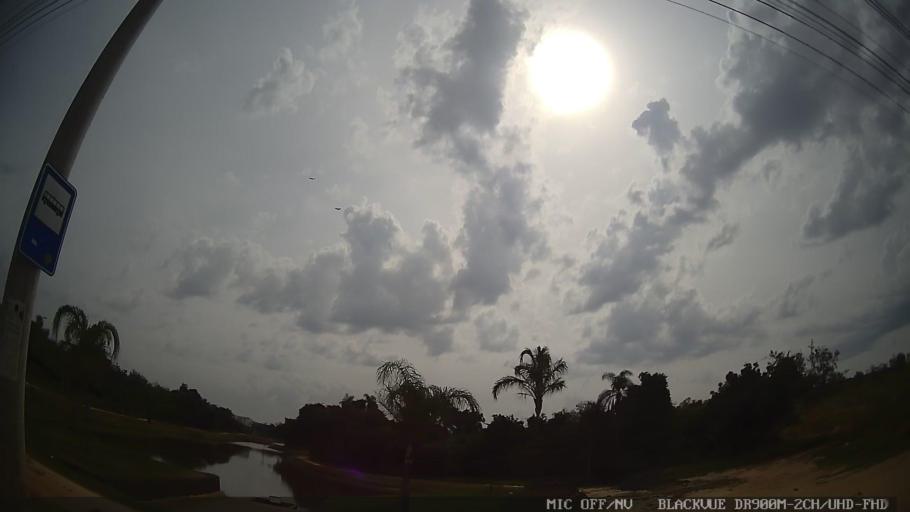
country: BR
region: Sao Paulo
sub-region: Indaiatuba
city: Indaiatuba
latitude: -23.1039
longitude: -47.2663
